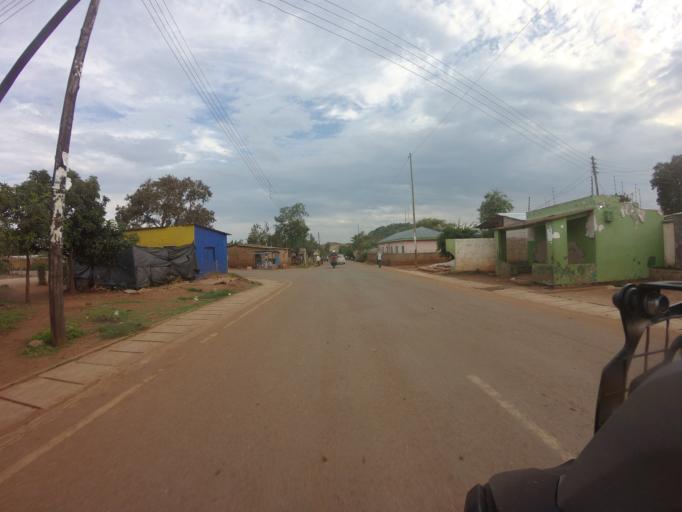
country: ZM
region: Lusaka
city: Lusaka
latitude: -15.5378
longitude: 28.2380
